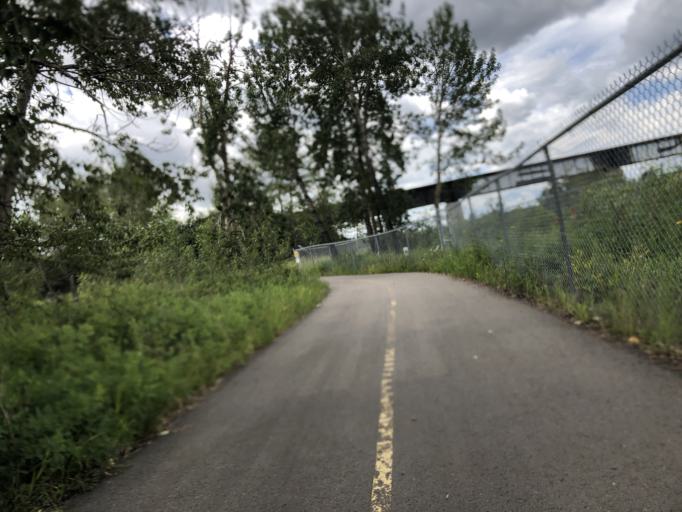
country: CA
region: Alberta
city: Calgary
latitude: 51.0048
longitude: -114.0200
